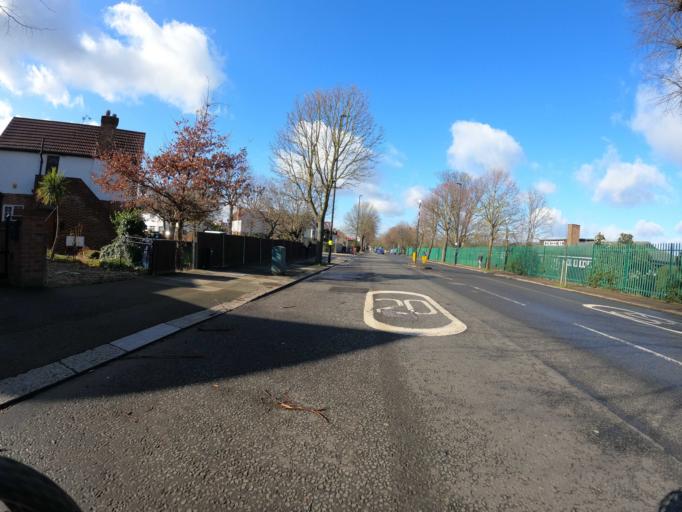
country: GB
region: England
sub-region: Greater London
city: Ealing Broadway
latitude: 51.5269
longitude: -0.3260
